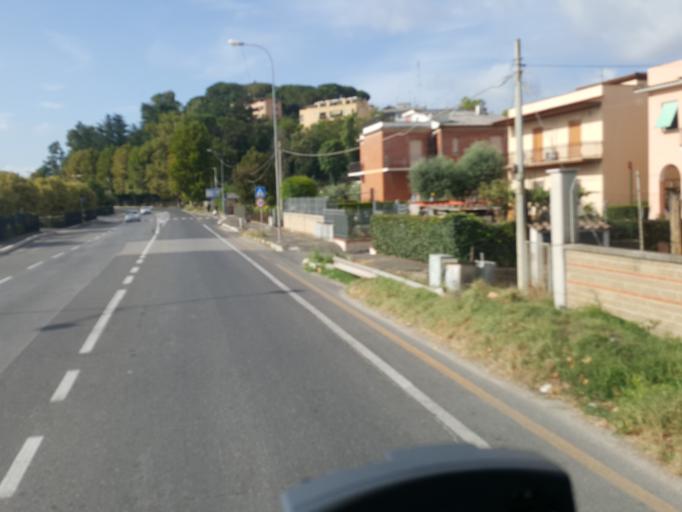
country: IT
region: Latium
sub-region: Citta metropolitana di Roma Capitale
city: Girardi-Bellavista-Terrazze
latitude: 42.1066
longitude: 12.5831
